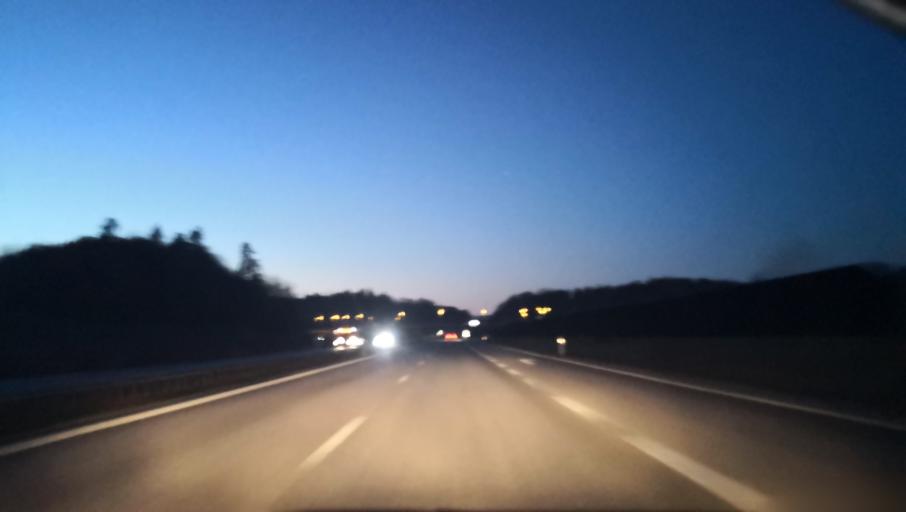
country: SE
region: Stockholm
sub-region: Nynashamns Kommun
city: Osmo
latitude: 58.9728
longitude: 17.9106
